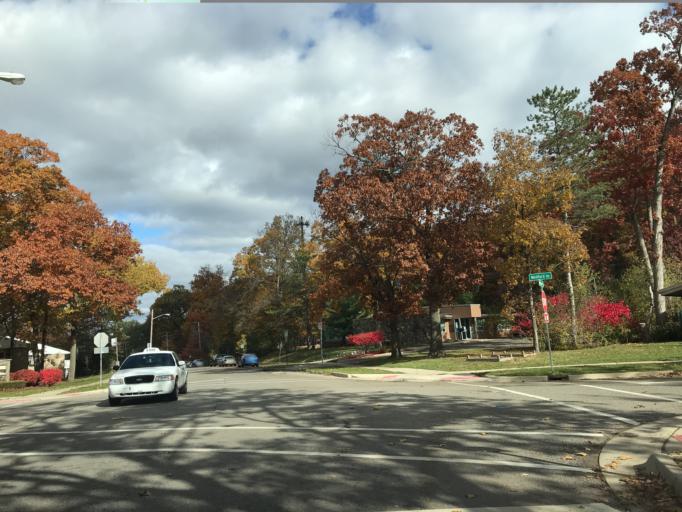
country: US
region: Michigan
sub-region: Washtenaw County
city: Ann Arbor
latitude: 42.2565
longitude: -83.7112
